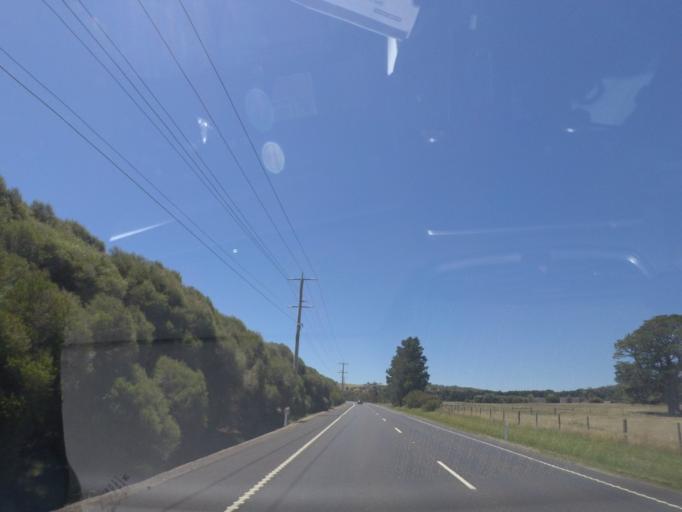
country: AU
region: Victoria
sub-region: Whittlesea
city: Whittlesea
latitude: -37.4676
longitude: 145.0309
